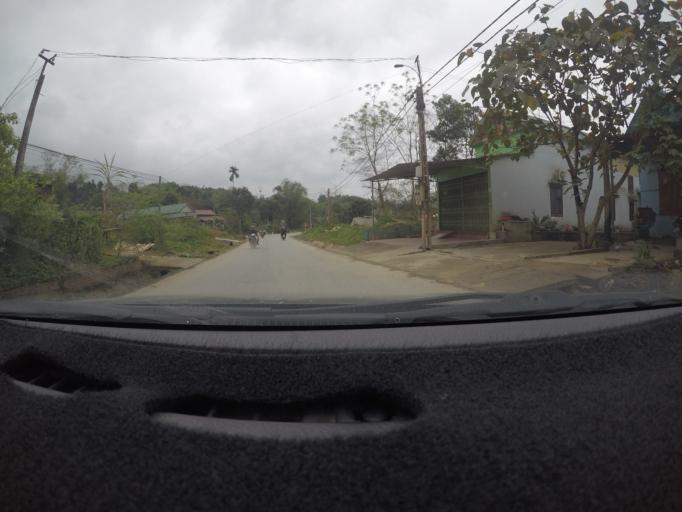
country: VN
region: Yen Bai
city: Co Phuc
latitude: 21.9188
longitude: 104.8045
